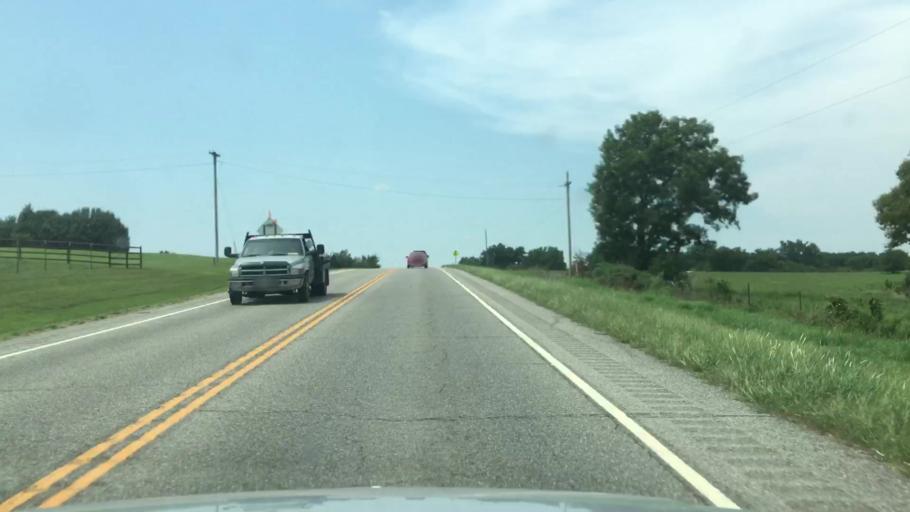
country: US
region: Oklahoma
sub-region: Muskogee County
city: Fort Gibson
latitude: 35.9369
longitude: -95.1917
